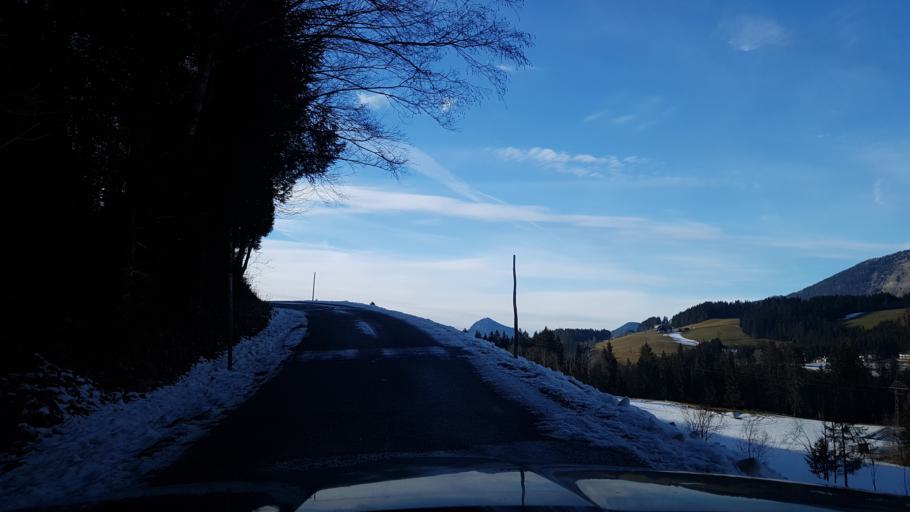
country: AT
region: Salzburg
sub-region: Politischer Bezirk Hallein
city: Abtenau
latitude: 47.5766
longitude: 13.4208
